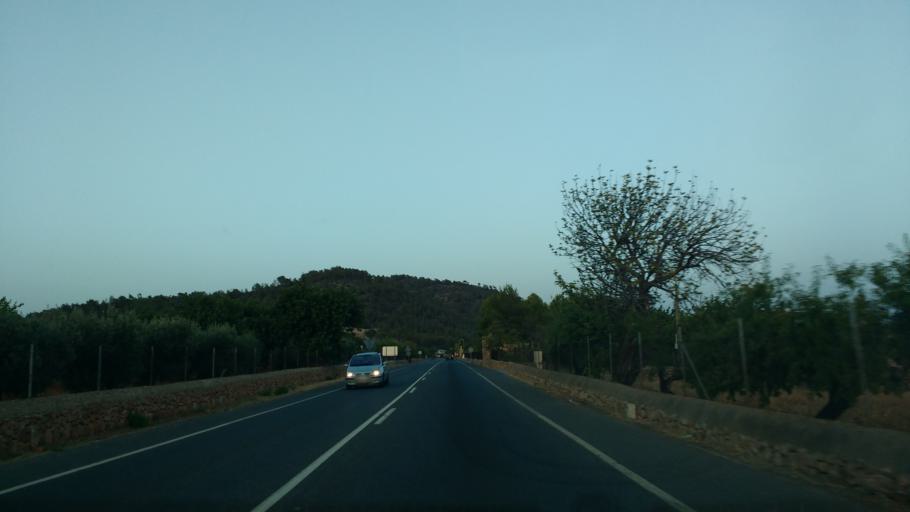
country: ES
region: Balearic Islands
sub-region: Illes Balears
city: Bunyola
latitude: 39.6674
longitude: 2.7062
